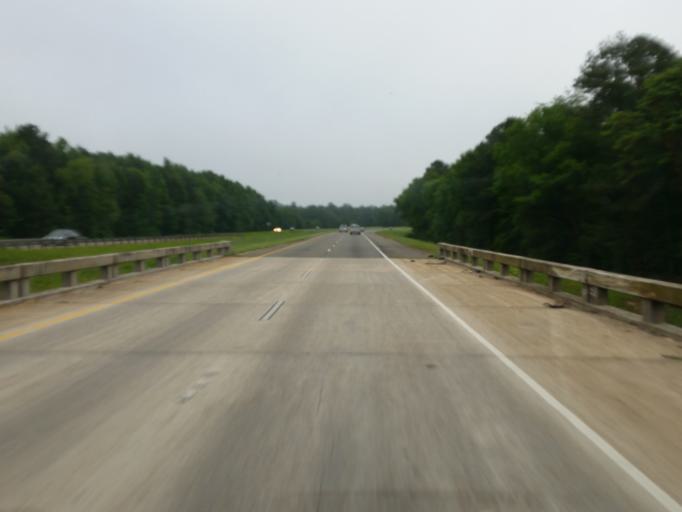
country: US
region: Louisiana
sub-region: Bossier Parish
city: Haughton
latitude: 32.5713
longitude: -93.4855
